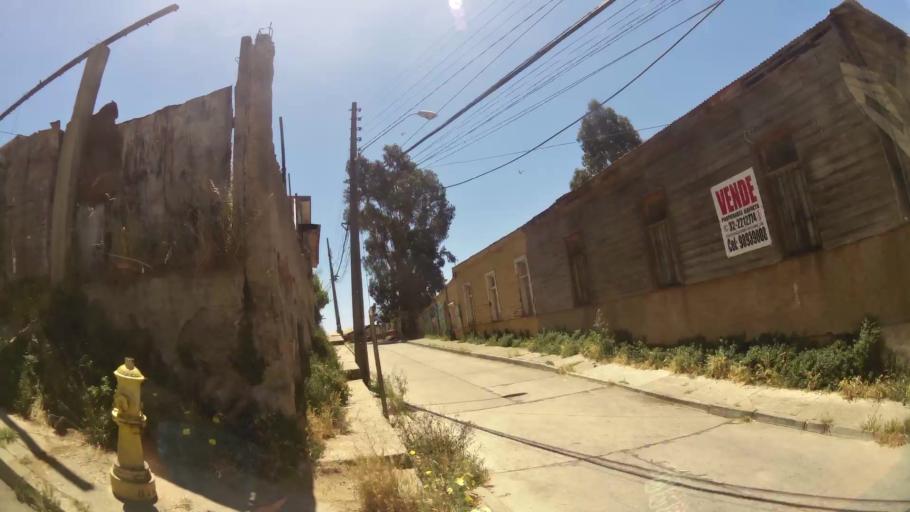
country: CL
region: Valparaiso
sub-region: Provincia de Valparaiso
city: Valparaiso
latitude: -33.0531
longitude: -71.6352
